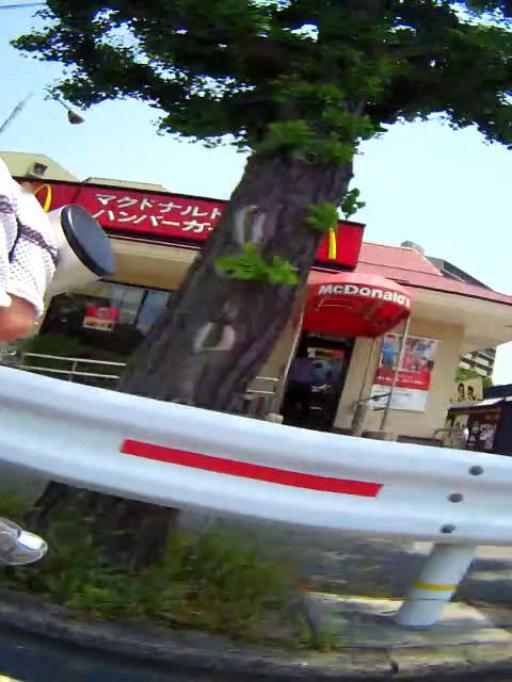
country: JP
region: Osaka
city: Toyonaka
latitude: 34.8030
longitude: 135.4932
